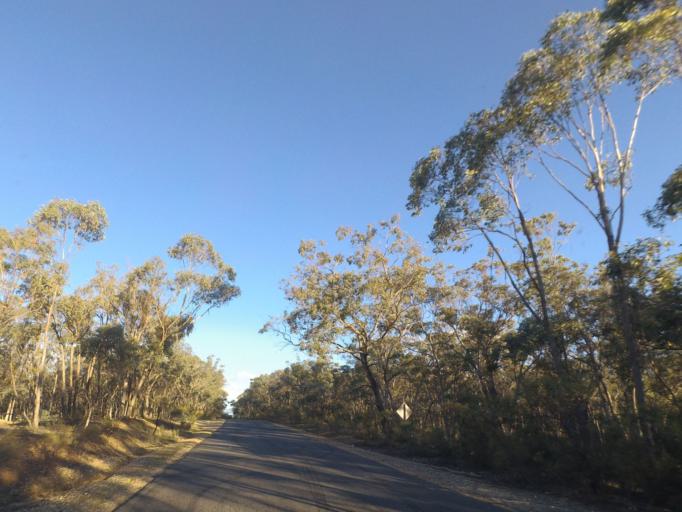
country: AU
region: Victoria
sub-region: Mount Alexander
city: Castlemaine
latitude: -37.1420
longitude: 144.2024
